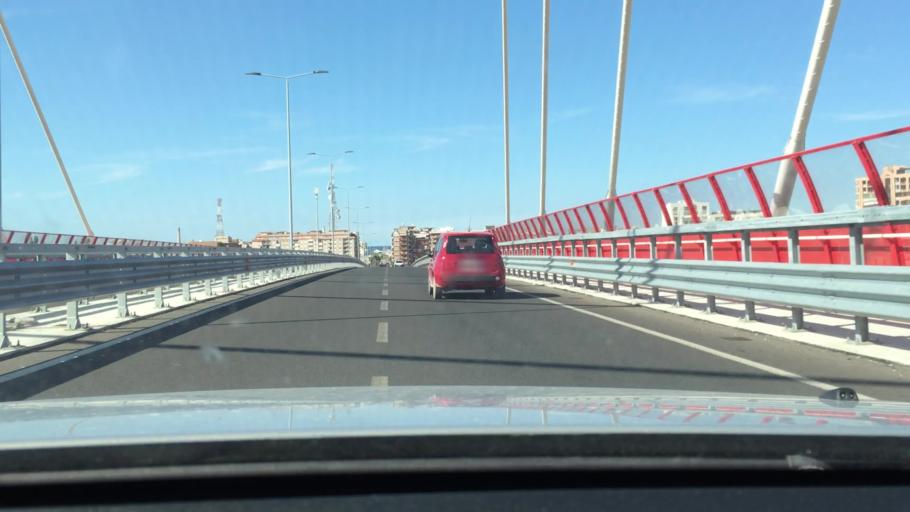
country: IT
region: Apulia
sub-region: Provincia di Bari
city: Bari
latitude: 41.1196
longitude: 16.8483
